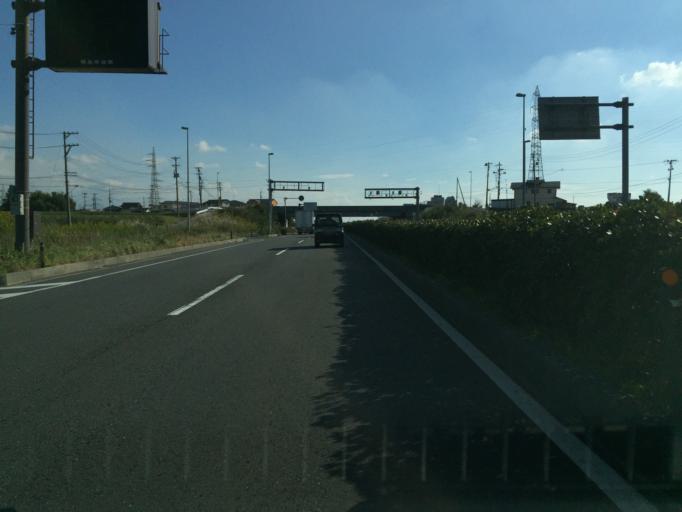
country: JP
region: Fukushima
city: Koriyama
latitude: 37.4533
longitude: 140.3787
